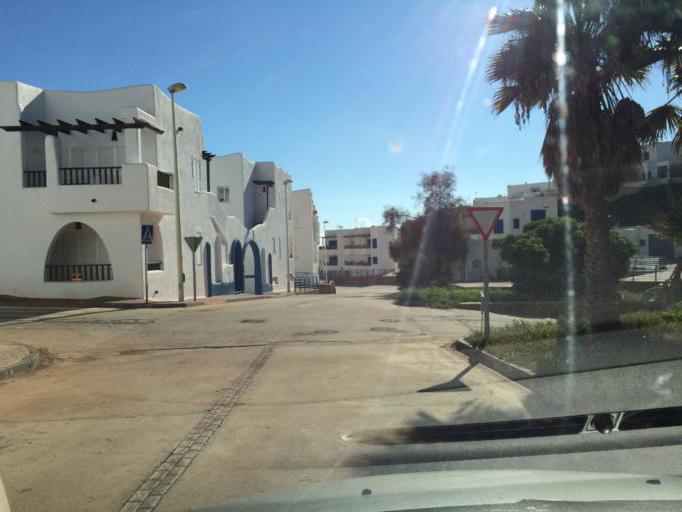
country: ES
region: Andalusia
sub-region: Provincia de Almeria
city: San Jose
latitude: 36.8154
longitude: -2.0530
